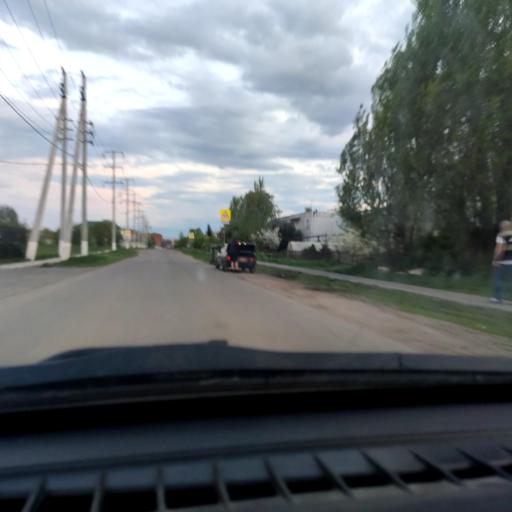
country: RU
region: Samara
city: Podstepki
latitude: 53.5189
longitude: 49.1128
